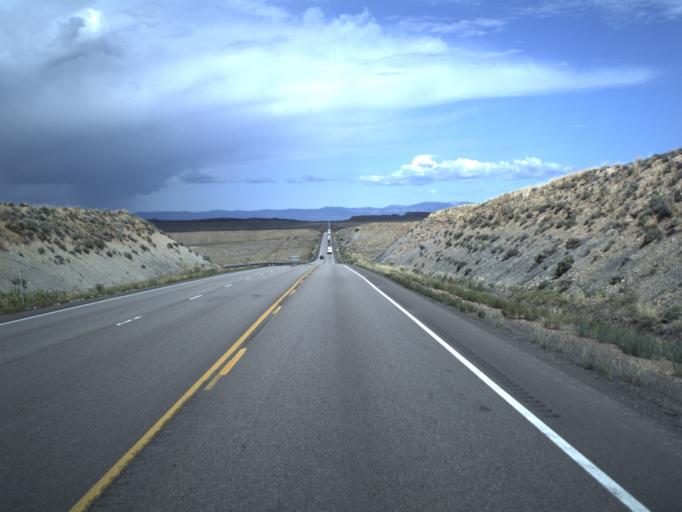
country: US
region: Utah
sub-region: Carbon County
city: East Carbon City
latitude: 39.5121
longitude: -110.5417
